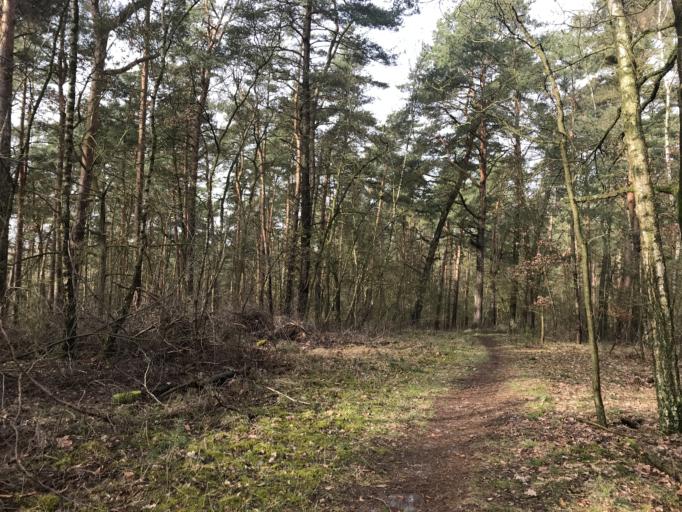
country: DE
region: Lower Saxony
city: Uelzen
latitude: 52.9505
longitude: 10.5619
